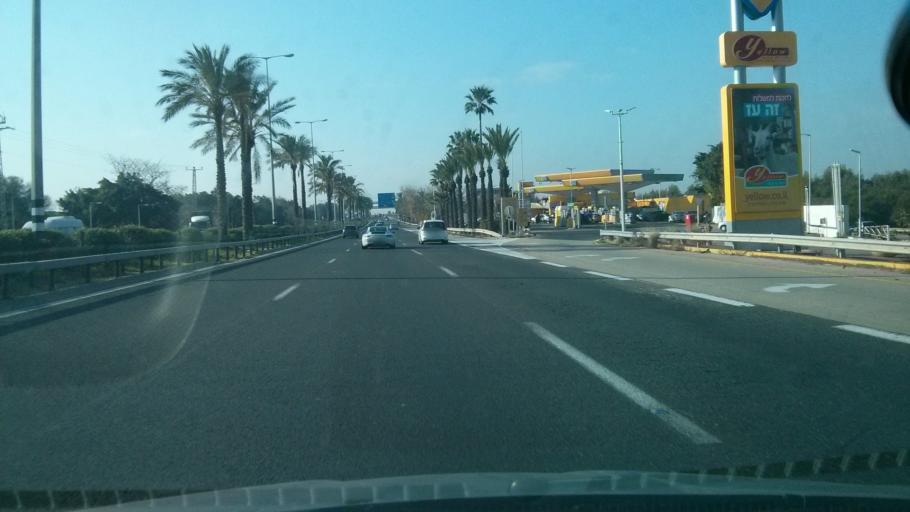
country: IL
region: Tel Aviv
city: Herzliya Pituah
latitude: 32.1572
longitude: 34.8091
